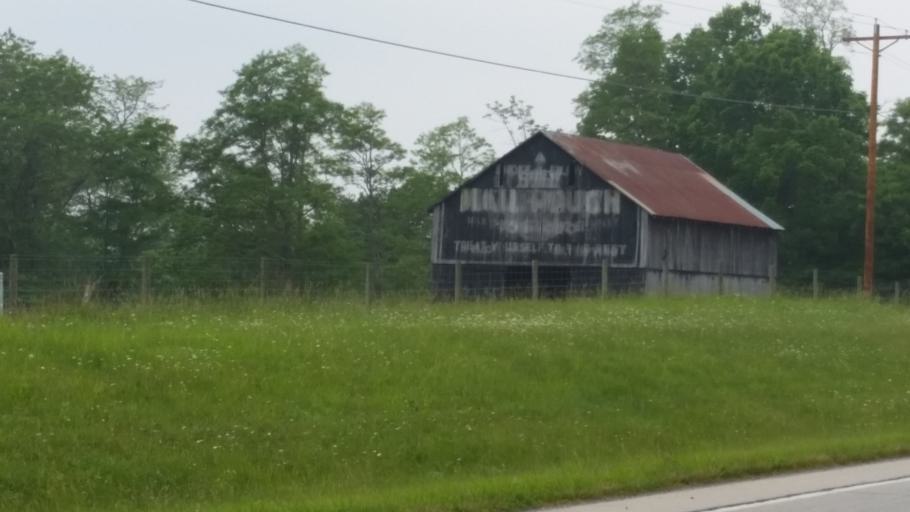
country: US
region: Ohio
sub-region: Highland County
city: Greenfield
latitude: 39.2281
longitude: -83.3824
